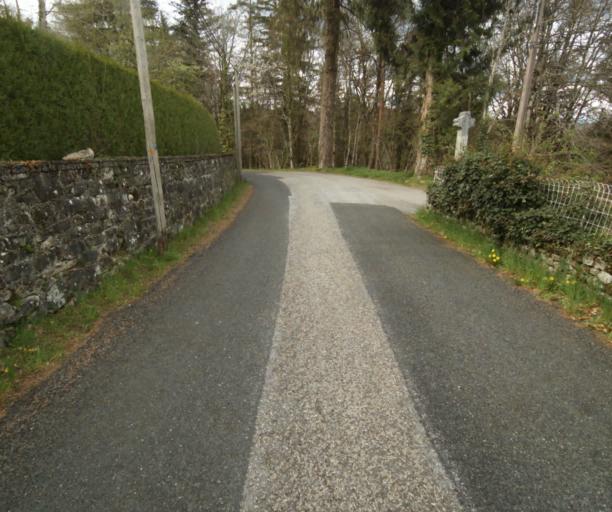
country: FR
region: Limousin
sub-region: Departement de la Correze
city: Argentat
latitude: 45.1971
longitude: 1.9691
